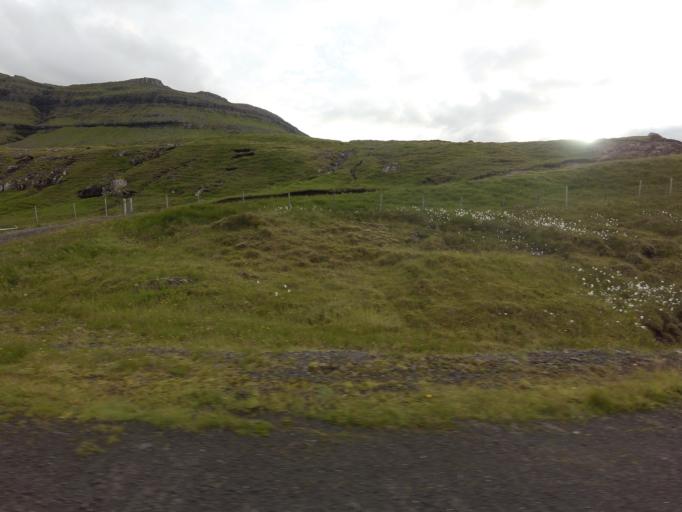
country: FO
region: Streymoy
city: Kollafjordhur
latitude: 62.1484
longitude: -6.9091
